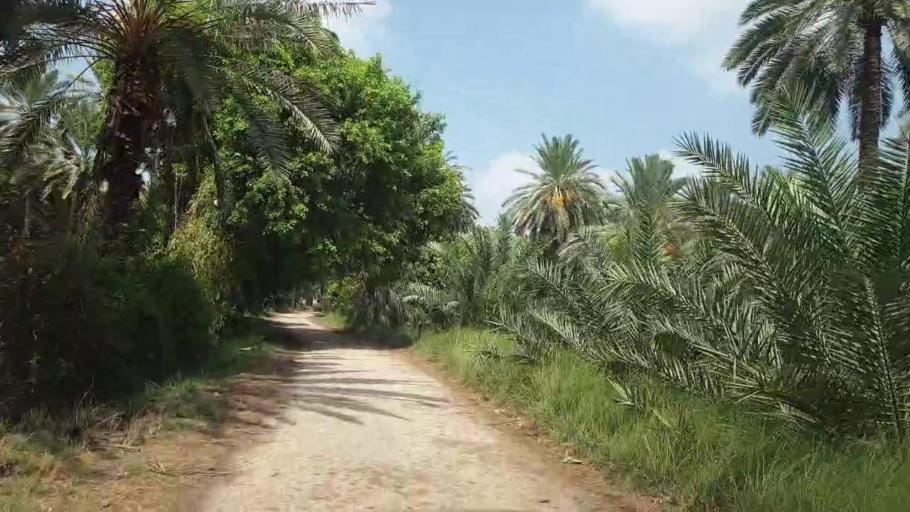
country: PK
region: Sindh
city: Pir jo Goth
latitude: 27.6095
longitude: 68.6692
